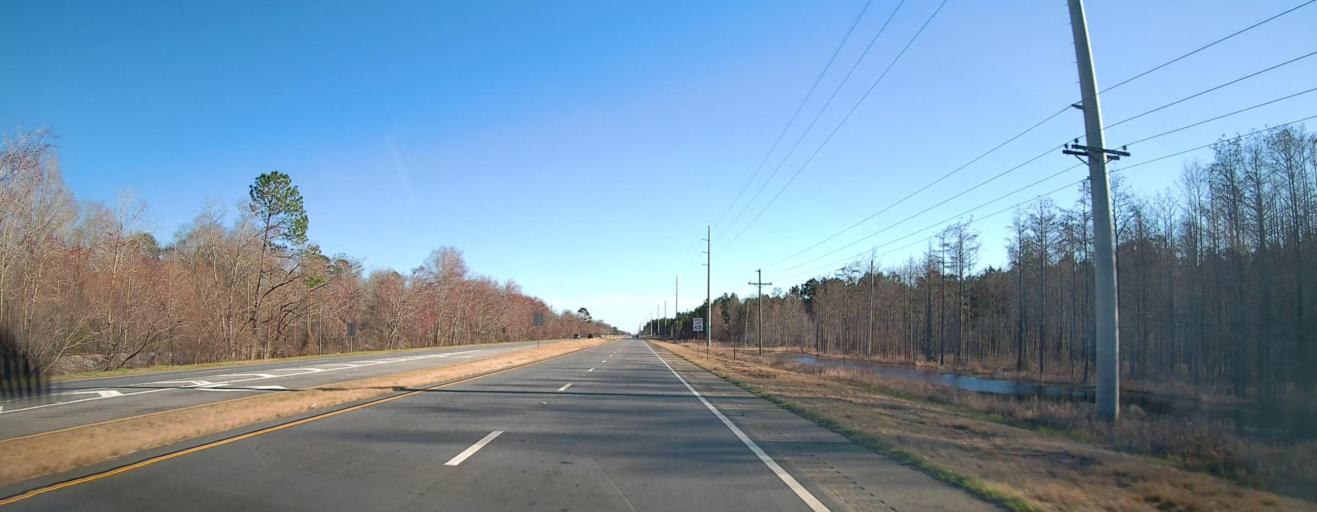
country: US
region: Georgia
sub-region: Lee County
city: Leesburg
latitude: 31.8822
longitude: -84.2435
